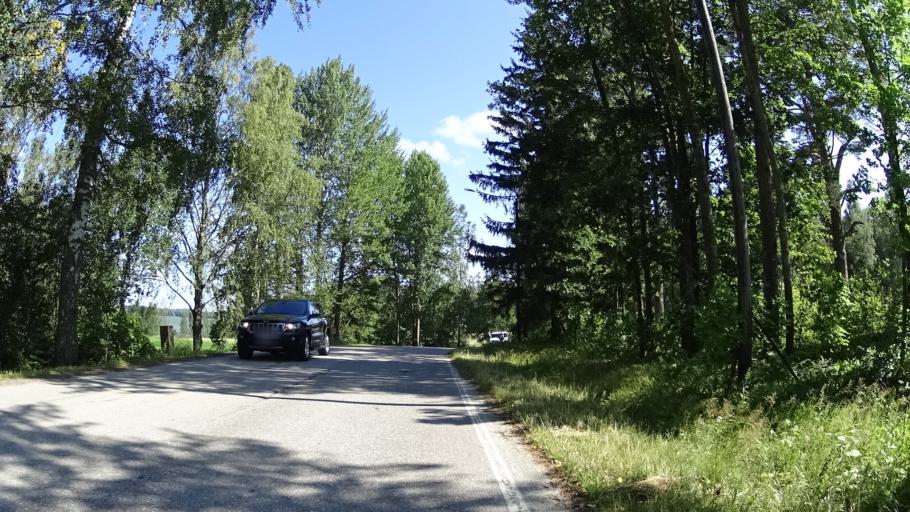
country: FI
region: Uusimaa
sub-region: Helsinki
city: Tuusula
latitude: 60.4338
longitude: 25.0574
